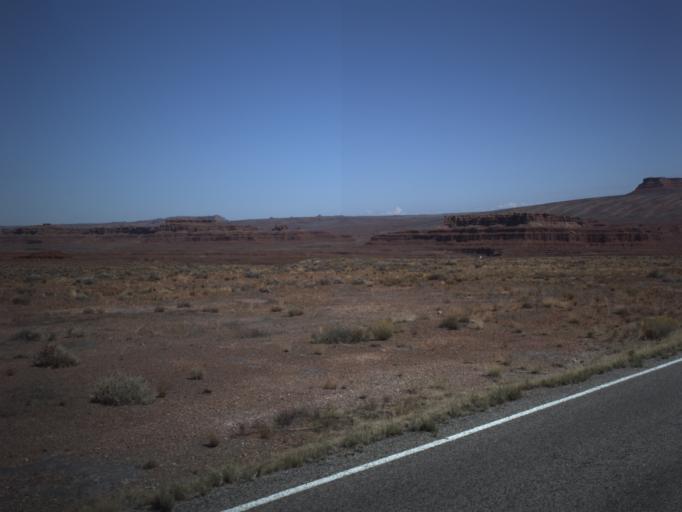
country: US
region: Utah
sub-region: San Juan County
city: Blanding
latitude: 37.1952
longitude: -109.8681
